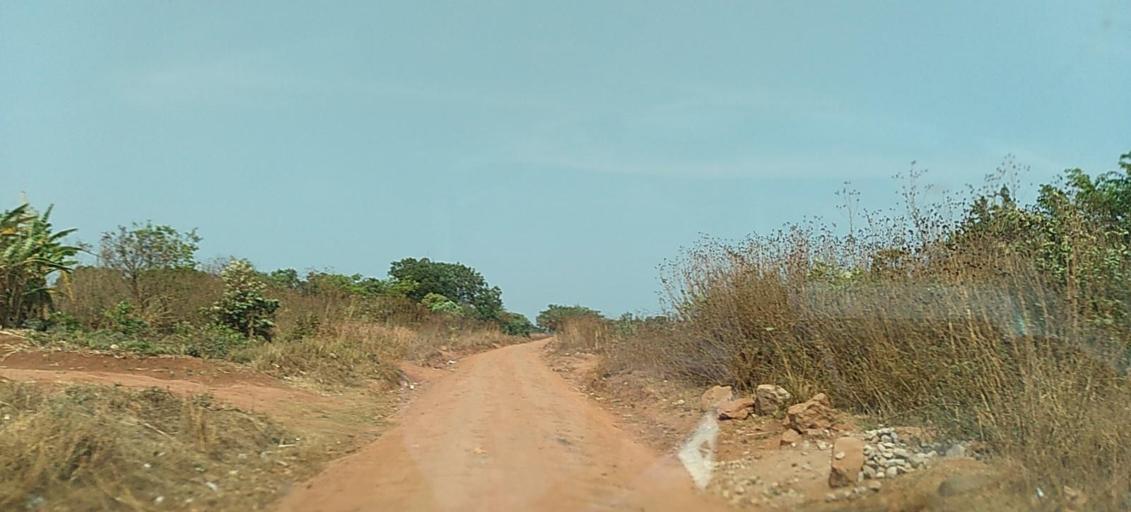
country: ZM
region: Copperbelt
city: Chililabombwe
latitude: -12.3421
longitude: 27.7077
